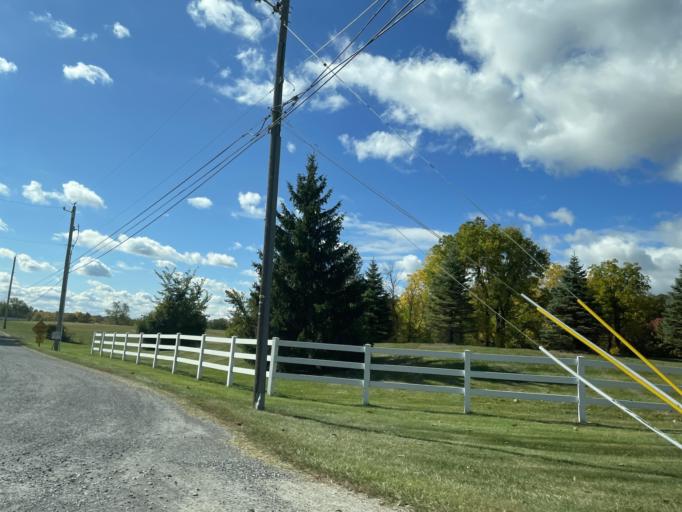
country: US
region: Indiana
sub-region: Allen County
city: Fort Wayne
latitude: 41.1078
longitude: -85.2162
